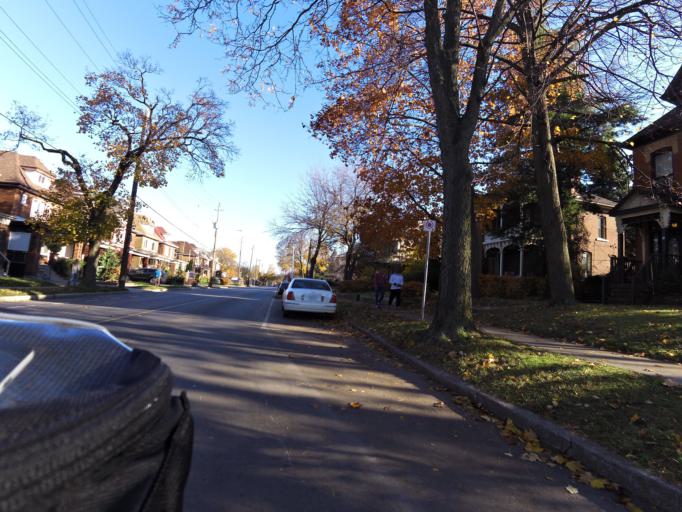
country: CA
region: Ontario
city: Hamilton
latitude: 43.2458
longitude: -79.8392
